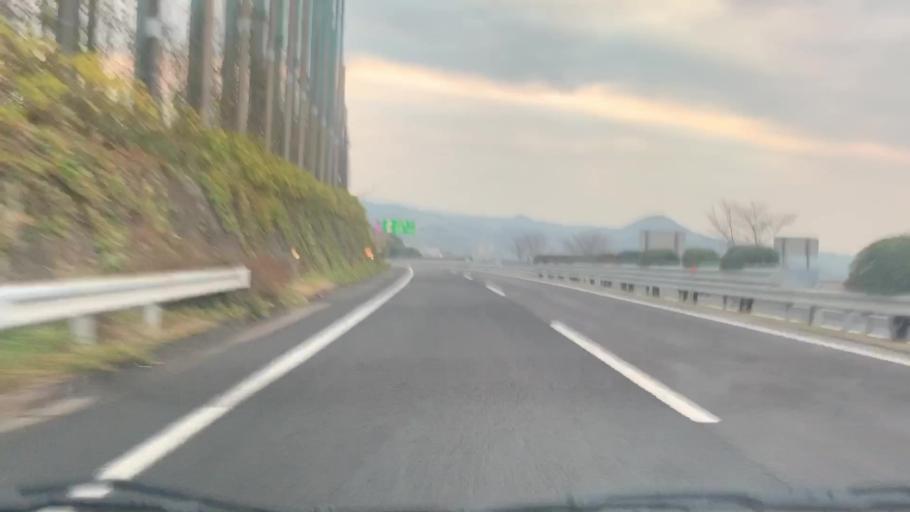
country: JP
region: Saga Prefecture
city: Ureshinomachi-shimojuku
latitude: 33.0298
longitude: 129.9306
